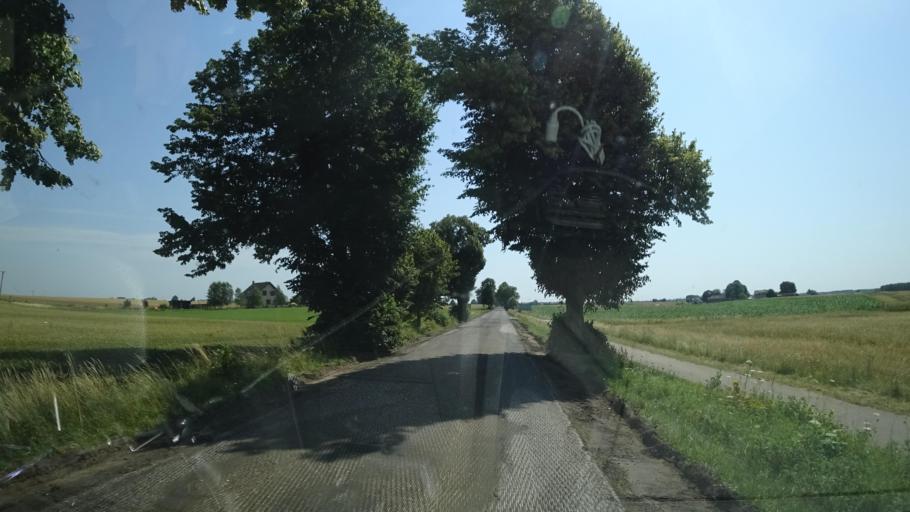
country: PL
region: Pomeranian Voivodeship
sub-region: Powiat chojnicki
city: Brusy
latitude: 53.8747
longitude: 17.6593
